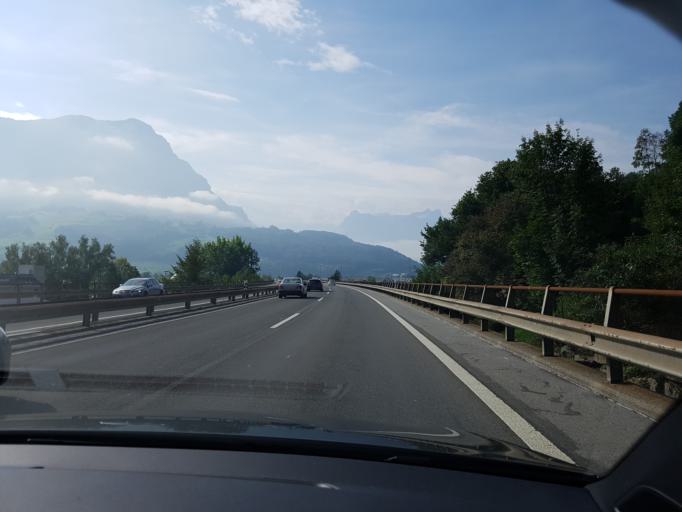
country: CH
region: Schwyz
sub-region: Bezirk Schwyz
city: Ingenbohl
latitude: 47.0194
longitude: 8.6267
